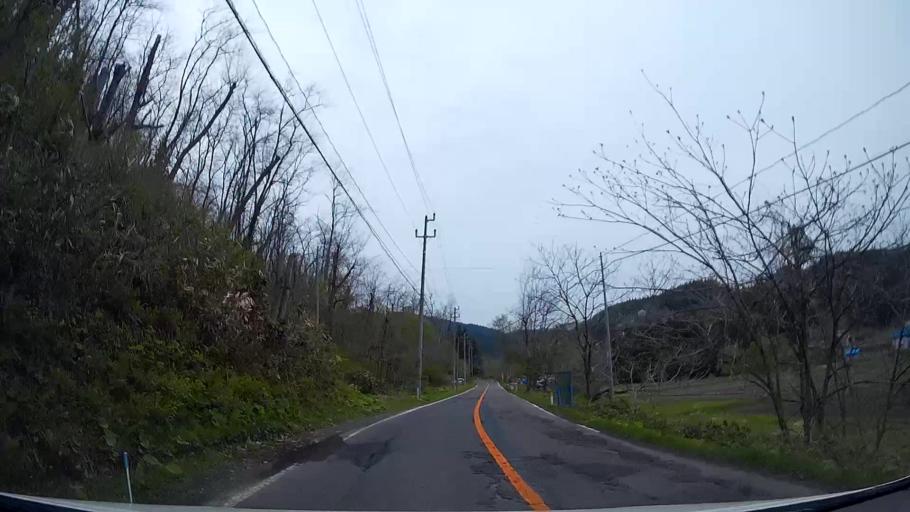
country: JP
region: Akita
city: Hanawa
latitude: 40.3111
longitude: 140.8357
